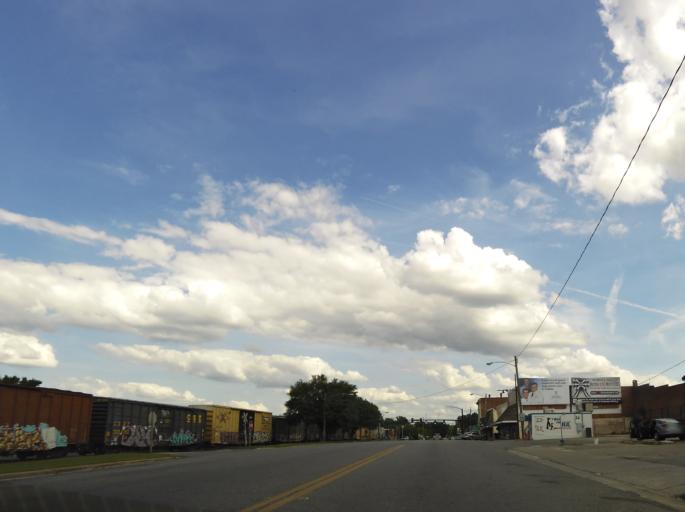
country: US
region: Georgia
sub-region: Treutlen County
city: Soperton
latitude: 32.3786
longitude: -82.5935
